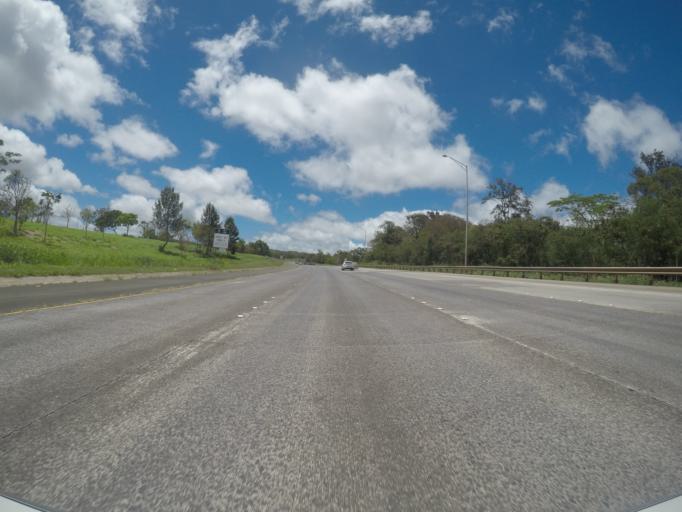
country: US
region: Hawaii
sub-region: Honolulu County
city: Mililani Town
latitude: 21.4373
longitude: -157.9940
